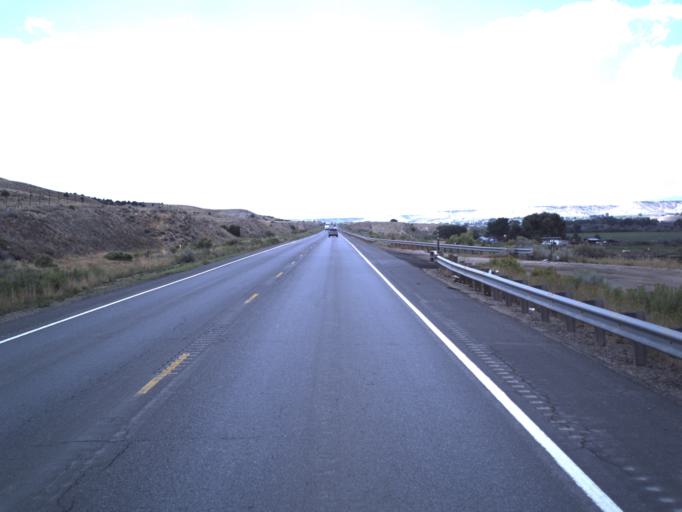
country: US
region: Utah
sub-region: Duchesne County
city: Duchesne
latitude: 40.1616
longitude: -110.2741
